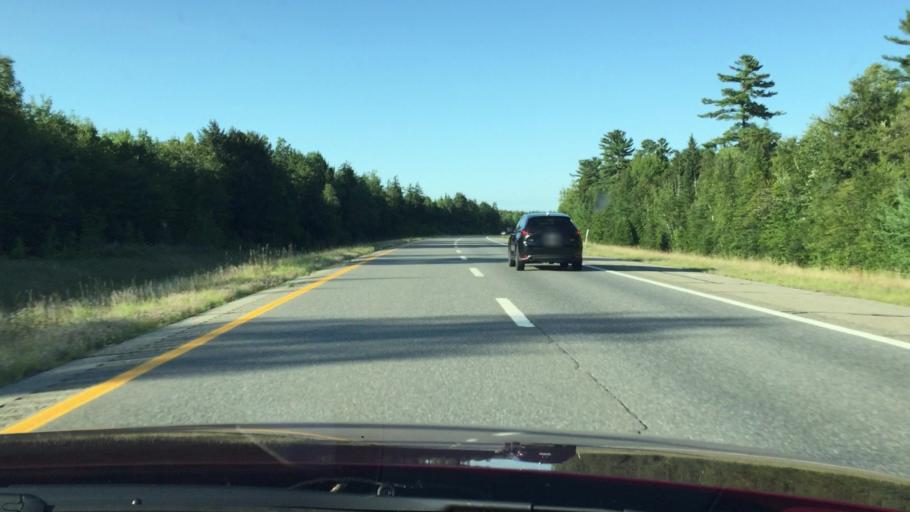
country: US
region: Maine
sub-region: Penobscot County
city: Lincoln
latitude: 45.4564
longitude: -68.5900
